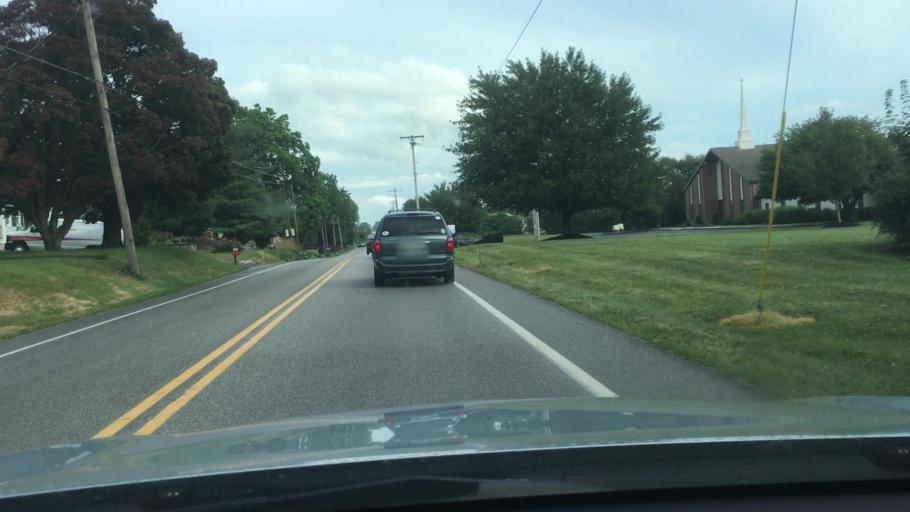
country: US
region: Pennsylvania
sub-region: Cumberland County
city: Carlisle
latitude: 40.1898
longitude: -77.1567
